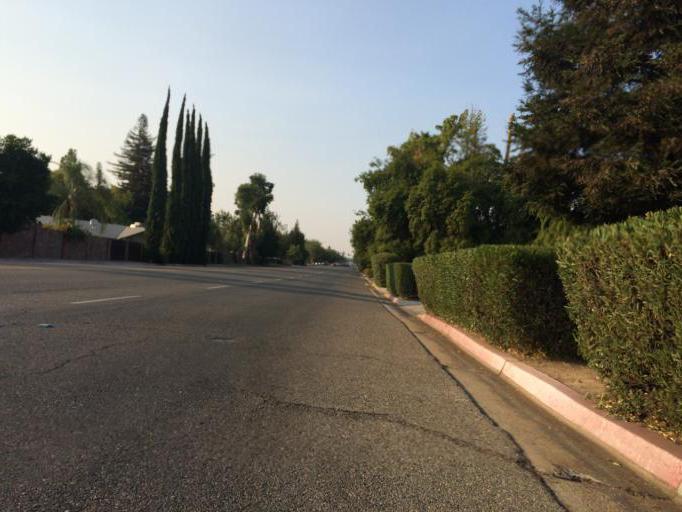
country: US
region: California
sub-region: Fresno County
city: Fresno
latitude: 36.8201
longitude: -119.8173
